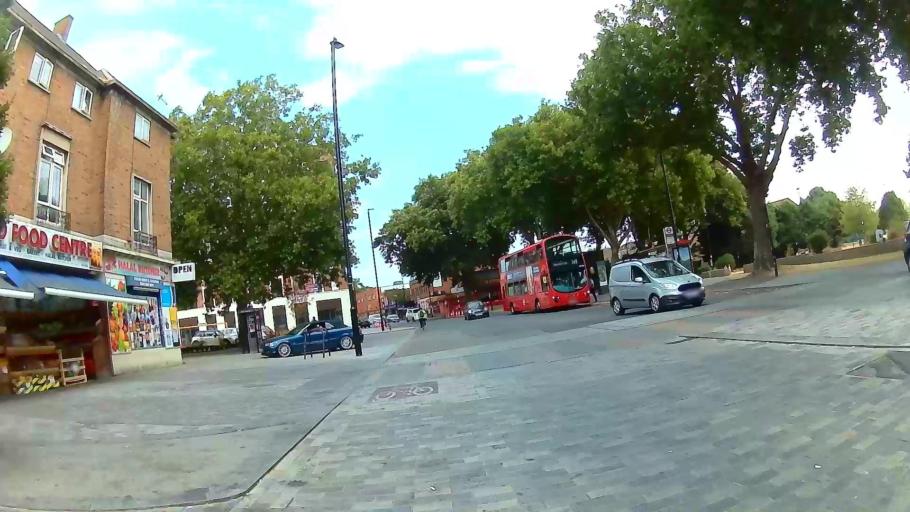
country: GB
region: England
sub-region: Greater London
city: Enfield
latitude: 51.6445
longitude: -0.0465
